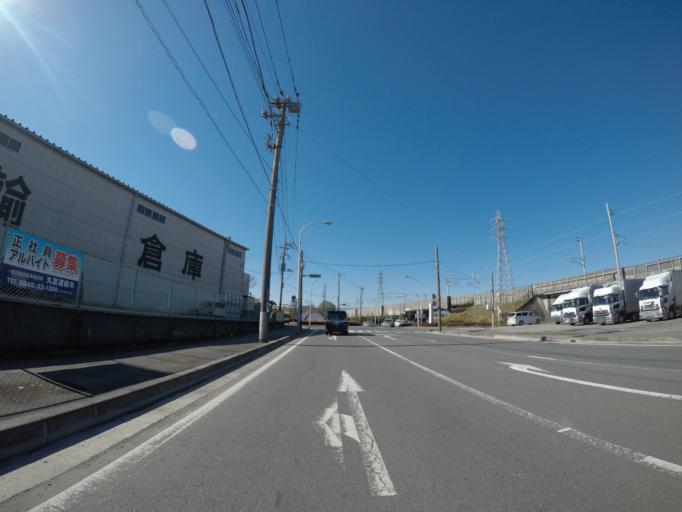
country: JP
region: Shizuoka
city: Fuji
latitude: 35.1512
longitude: 138.7154
